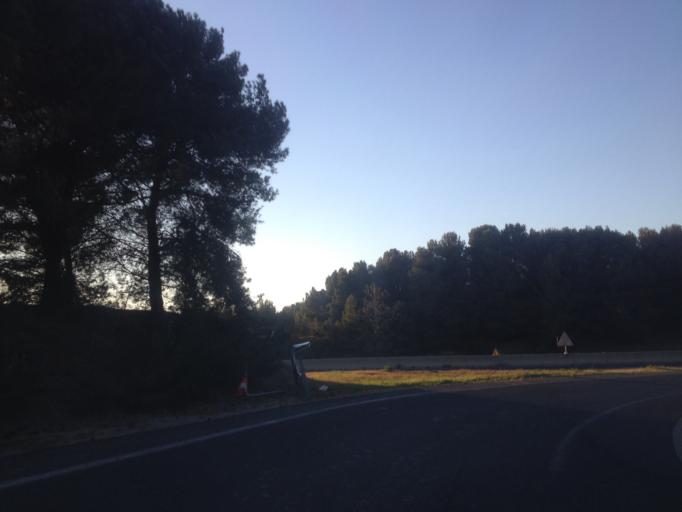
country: FR
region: Languedoc-Roussillon
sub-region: Departement de l'Herault
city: Le Cres
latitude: 43.6055
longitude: 3.9330
